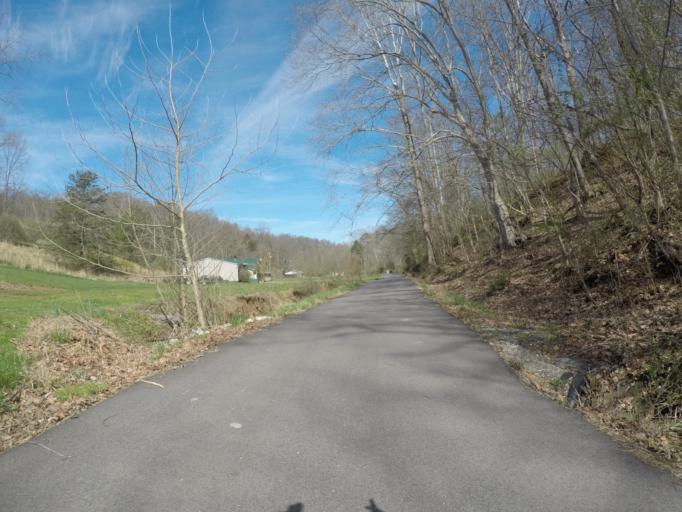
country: US
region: West Virginia
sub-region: Cabell County
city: Pea Ridge
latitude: 38.3911
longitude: -82.3481
